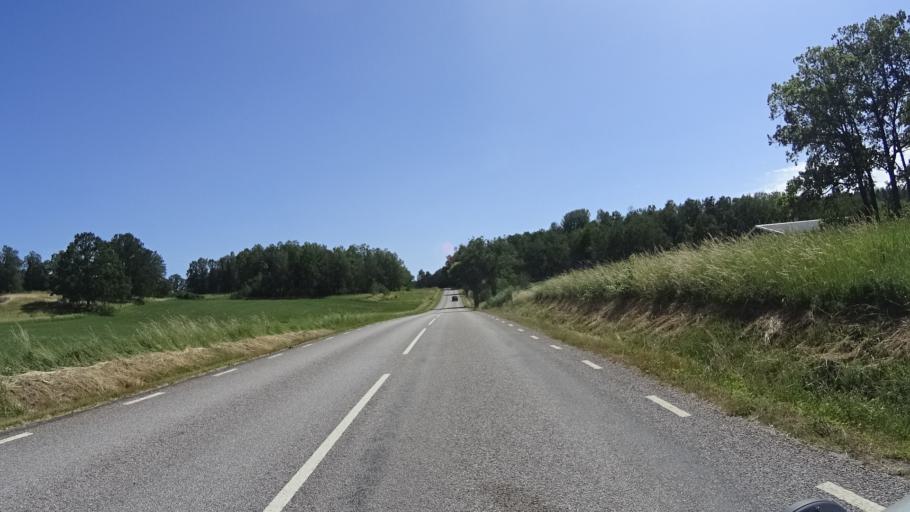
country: SE
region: Kalmar
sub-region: Vasterviks Kommun
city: Gamleby
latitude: 57.9132
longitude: 16.4118
